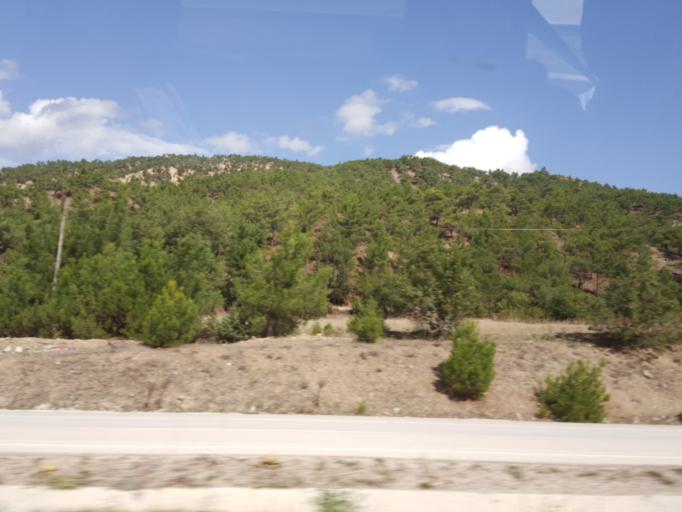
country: TR
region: Tokat
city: Resadiye
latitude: 40.3542
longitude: 37.4710
